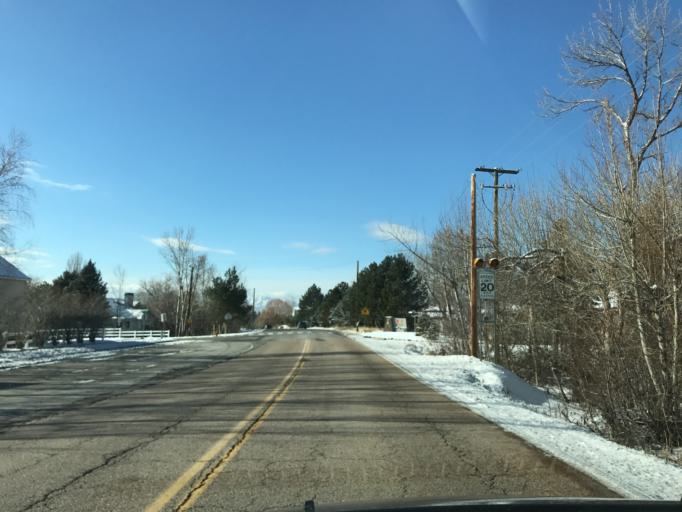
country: US
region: Utah
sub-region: Davis County
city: Fruit Heights
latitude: 41.0415
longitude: -111.9134
